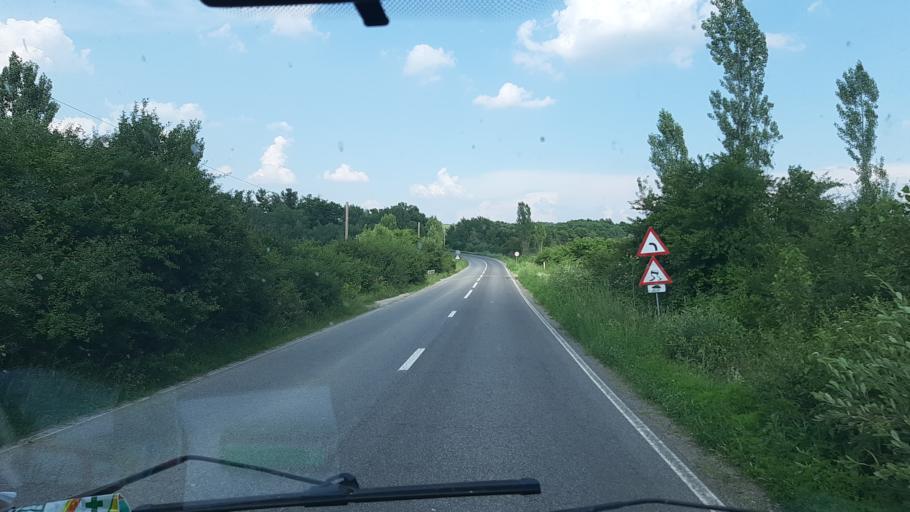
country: RO
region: Caras-Severin
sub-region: Comuna Farliug
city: Farliug
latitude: 45.5027
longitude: 21.8679
